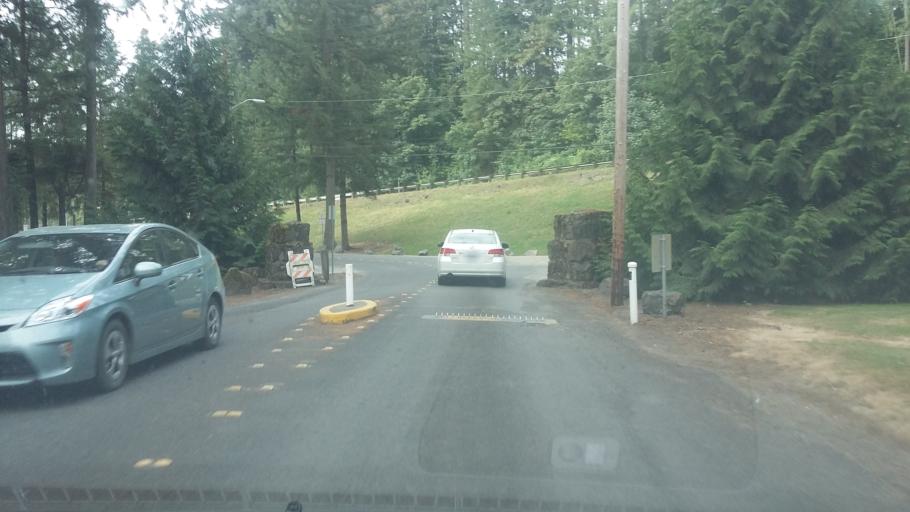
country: US
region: Washington
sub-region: Clark County
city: Lewisville
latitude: 45.8135
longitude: -122.5469
